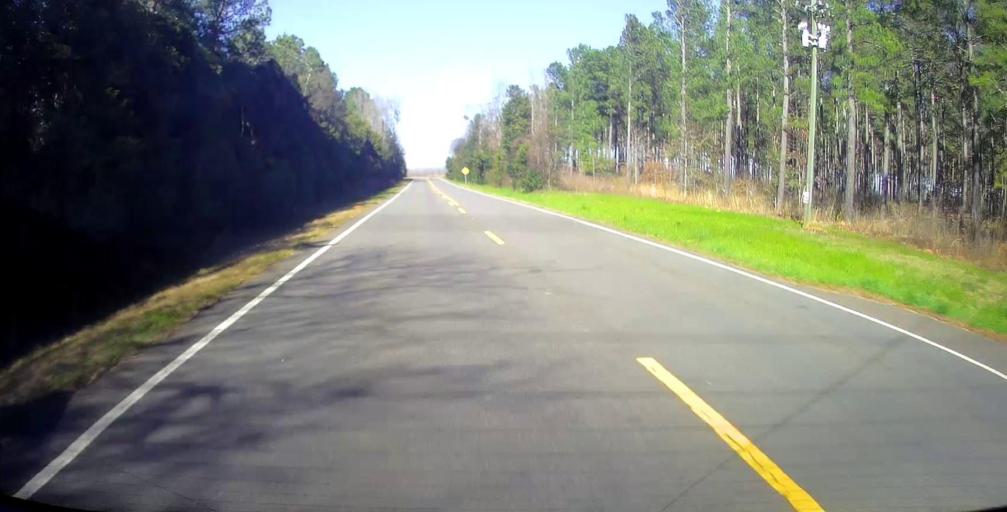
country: US
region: Georgia
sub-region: Macon County
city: Montezuma
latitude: 32.3643
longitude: -84.0136
